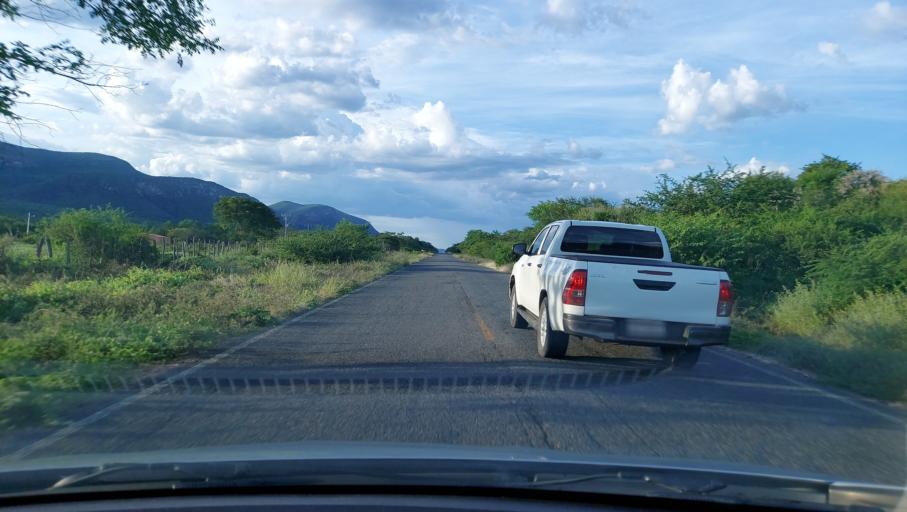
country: BR
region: Bahia
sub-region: Oliveira Dos Brejinhos
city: Beira Rio
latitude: -12.1870
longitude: -42.5395
